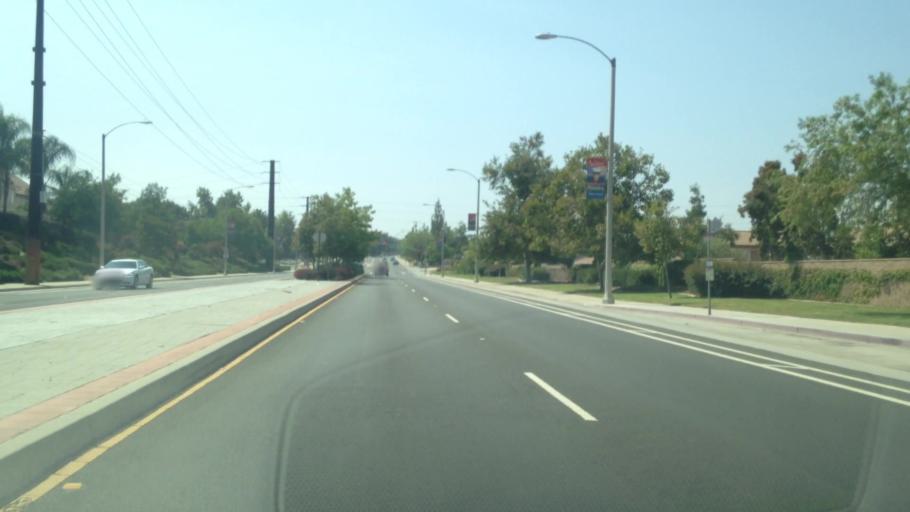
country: US
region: California
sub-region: Riverside County
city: Woodcrest
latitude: 33.9040
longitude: -117.3271
